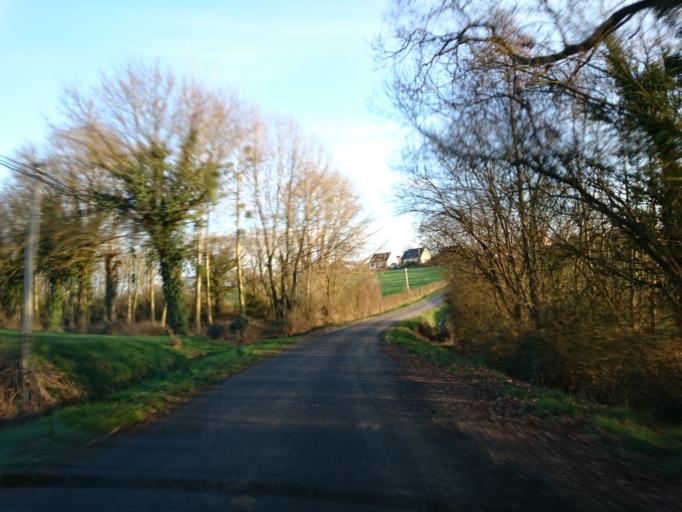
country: FR
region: Brittany
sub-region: Departement d'Ille-et-Vilaine
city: Chanteloup
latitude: 47.9240
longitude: -1.6077
